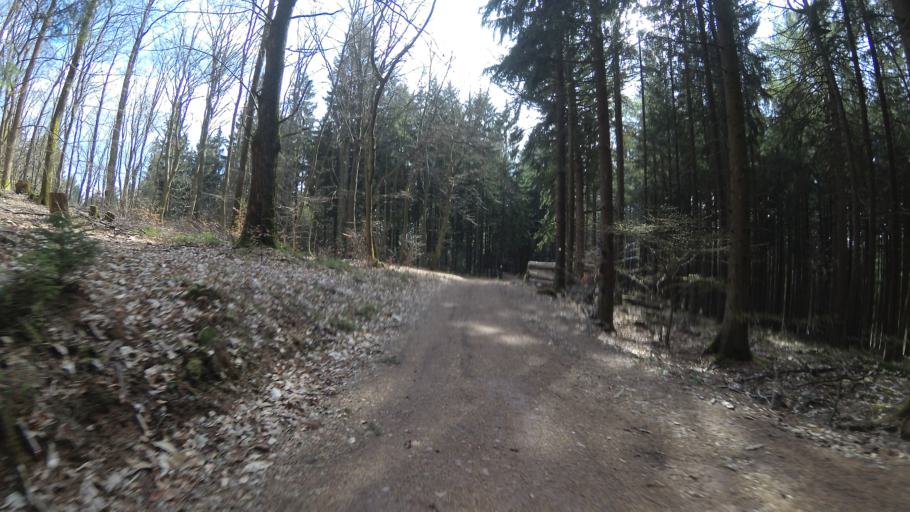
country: DE
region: Saarland
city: Tholey
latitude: 49.5275
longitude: 7.0236
